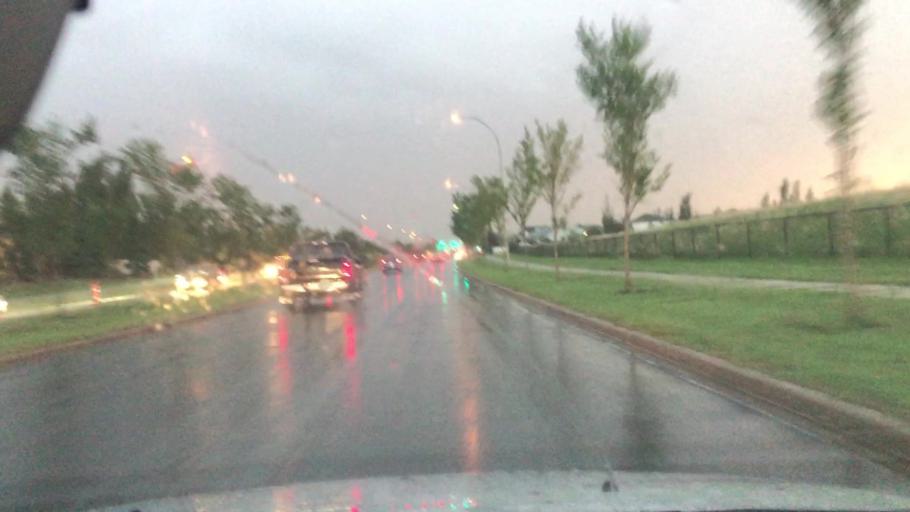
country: CA
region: Alberta
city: St. Albert
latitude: 53.6270
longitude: -113.5414
